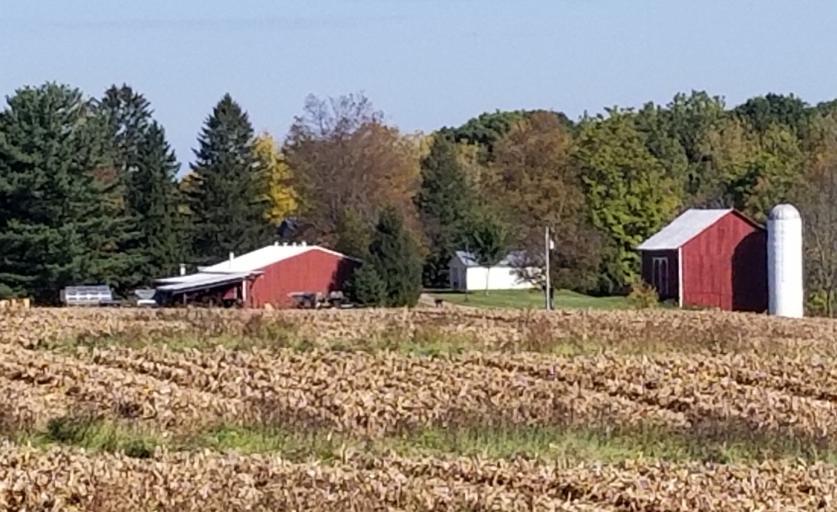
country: US
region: Ohio
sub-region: Crawford County
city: Galion
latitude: 40.6836
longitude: -82.7981
